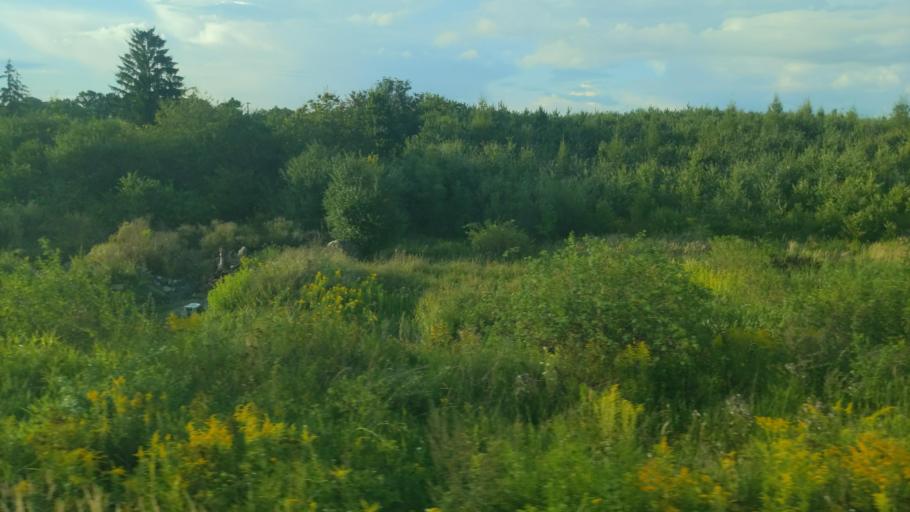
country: CZ
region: Praha
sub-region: Praha 20
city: Horni Pocernice
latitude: 50.0833
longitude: 14.6077
